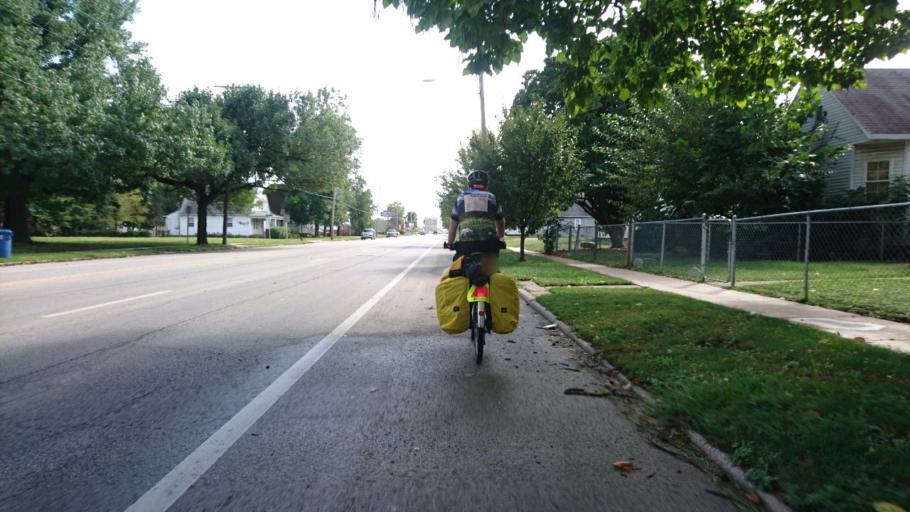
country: US
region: Illinois
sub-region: Sangamon County
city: Springfield
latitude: 39.8121
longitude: -89.6434
